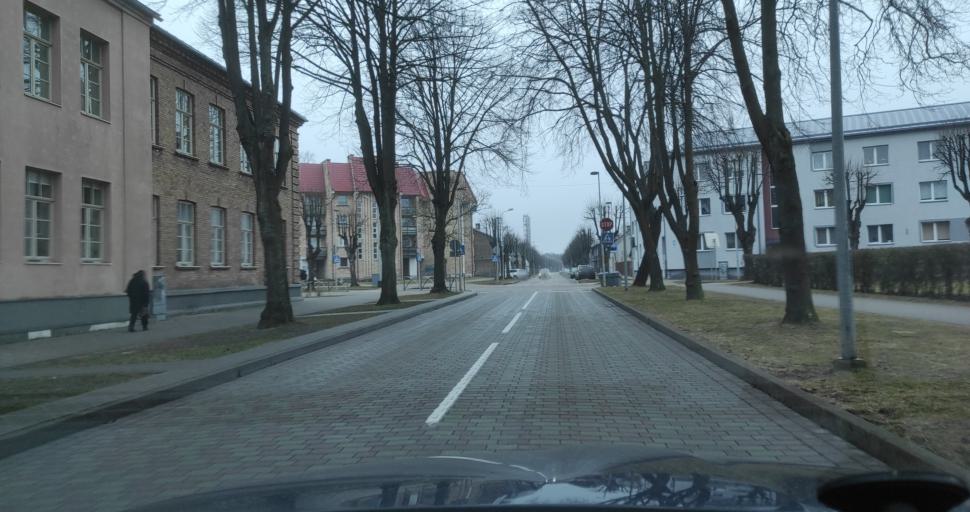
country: LV
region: Ventspils
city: Ventspils
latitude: 57.3884
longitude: 21.5589
